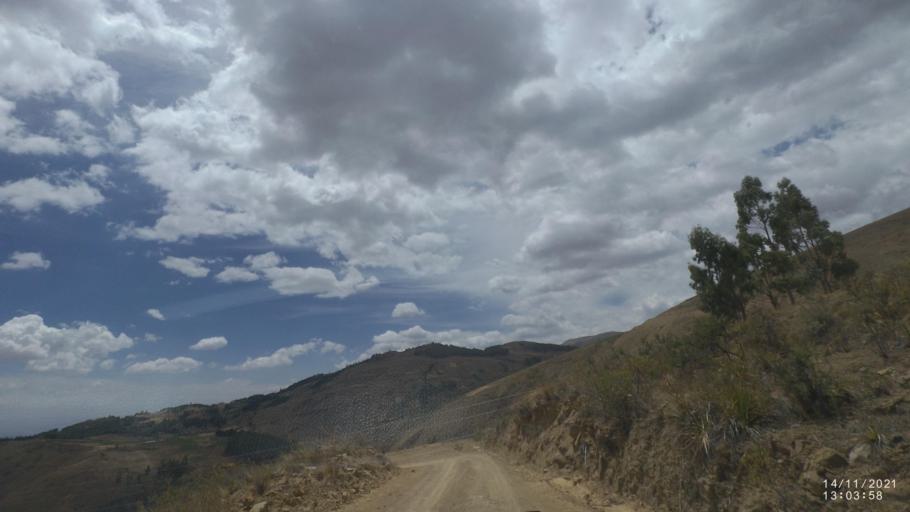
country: BO
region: Cochabamba
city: Colomi
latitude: -17.3705
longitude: -65.9785
